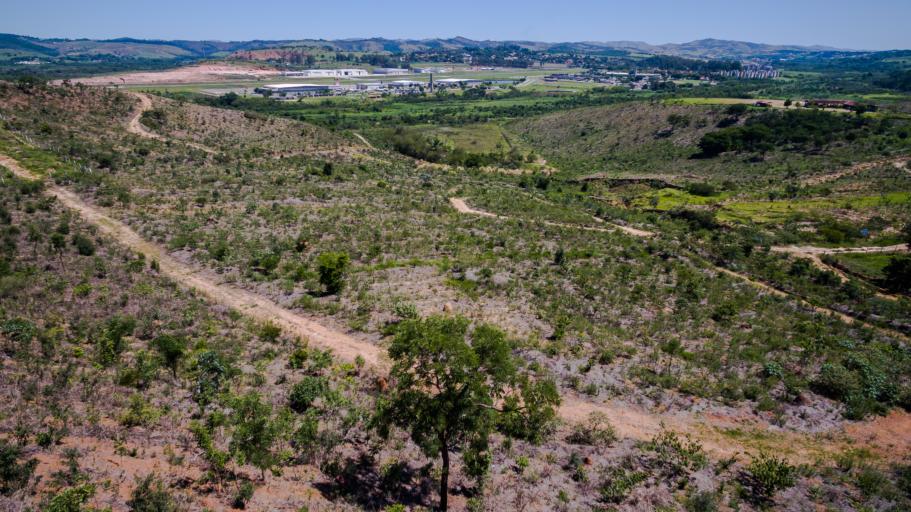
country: BR
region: Sao Paulo
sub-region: Taubate
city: Taubate
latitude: -23.0276
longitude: -45.5176
